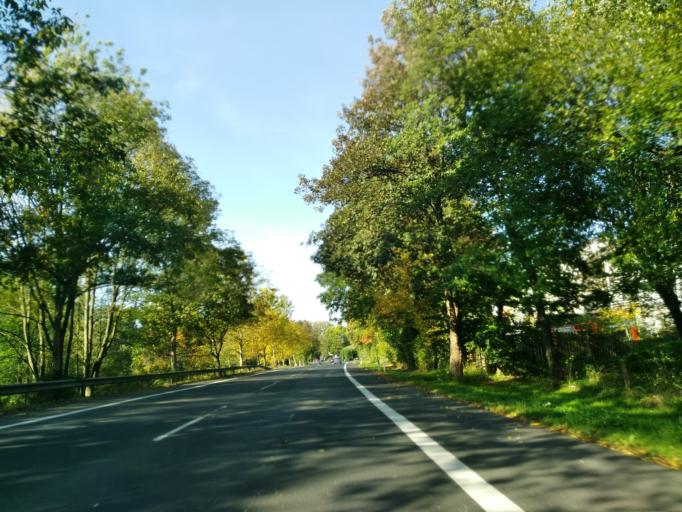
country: DE
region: North Rhine-Westphalia
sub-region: Regierungsbezirk Koln
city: Hennef
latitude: 50.7088
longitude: 7.2842
